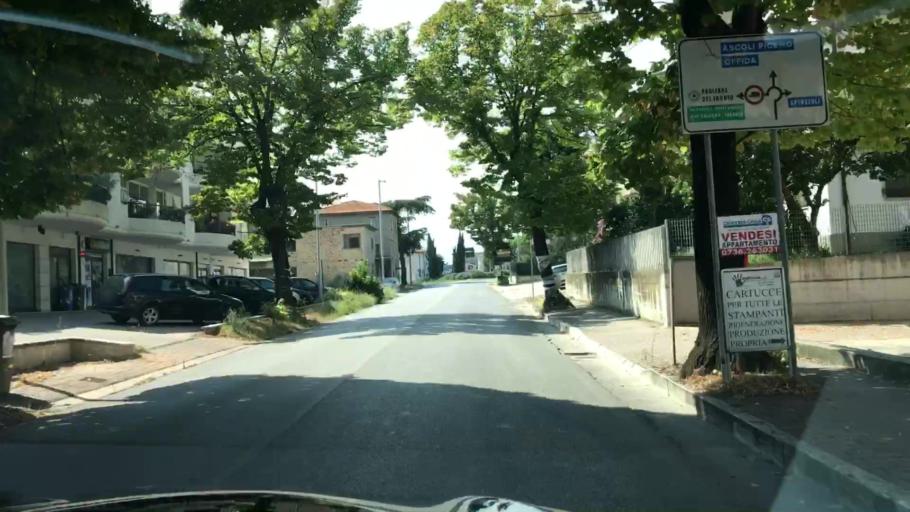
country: IT
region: The Marches
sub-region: Provincia di Ascoli Piceno
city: Pagliare
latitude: 42.8741
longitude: 13.7680
